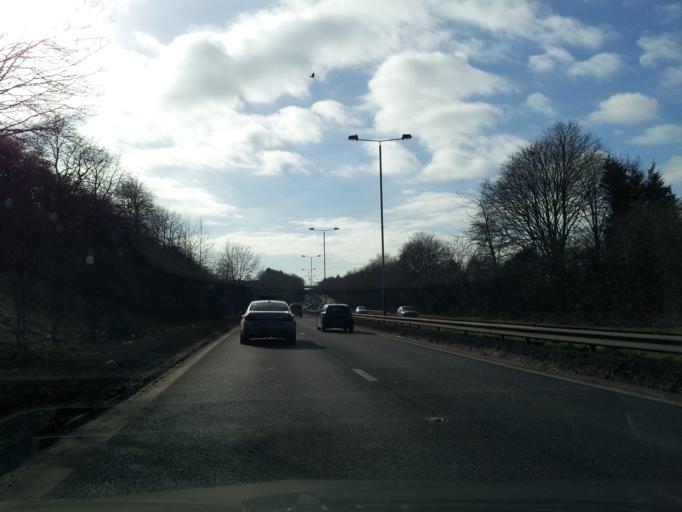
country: GB
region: England
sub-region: Derbyshire
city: Long Eaton
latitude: 52.9332
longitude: -1.2523
